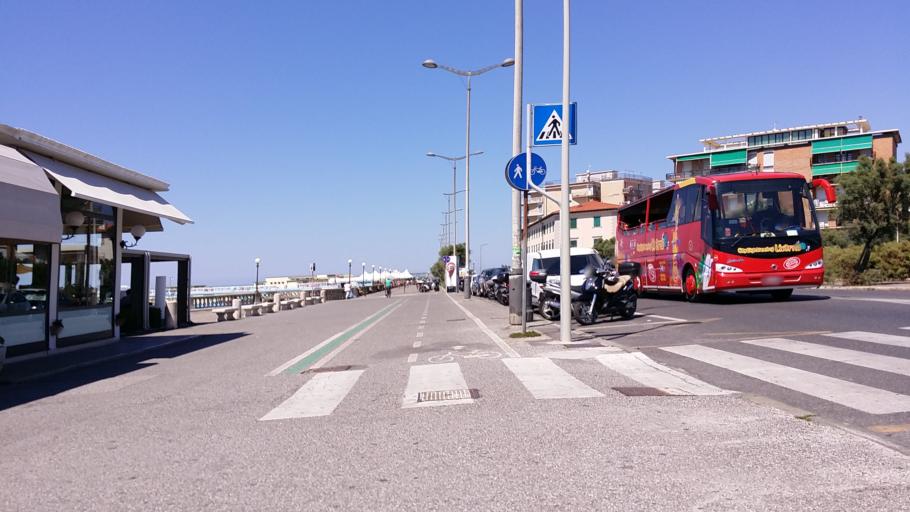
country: IT
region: Tuscany
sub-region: Provincia di Livorno
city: Livorno
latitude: 43.5301
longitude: 10.3058
